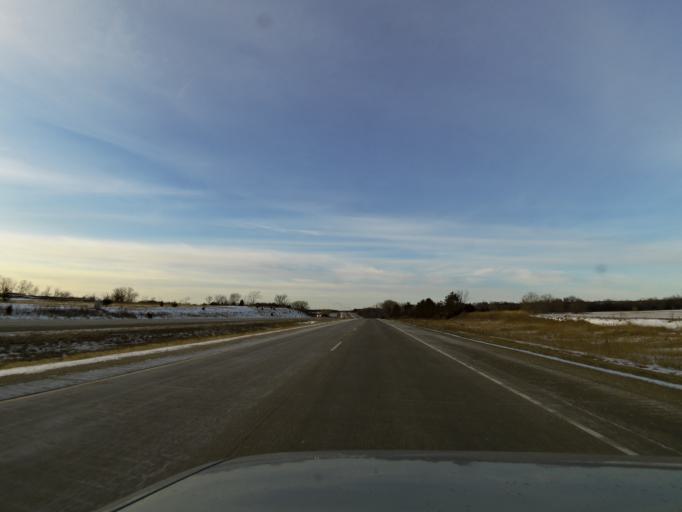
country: US
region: Wisconsin
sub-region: Pierce County
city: River Falls
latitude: 44.9148
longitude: -92.6679
